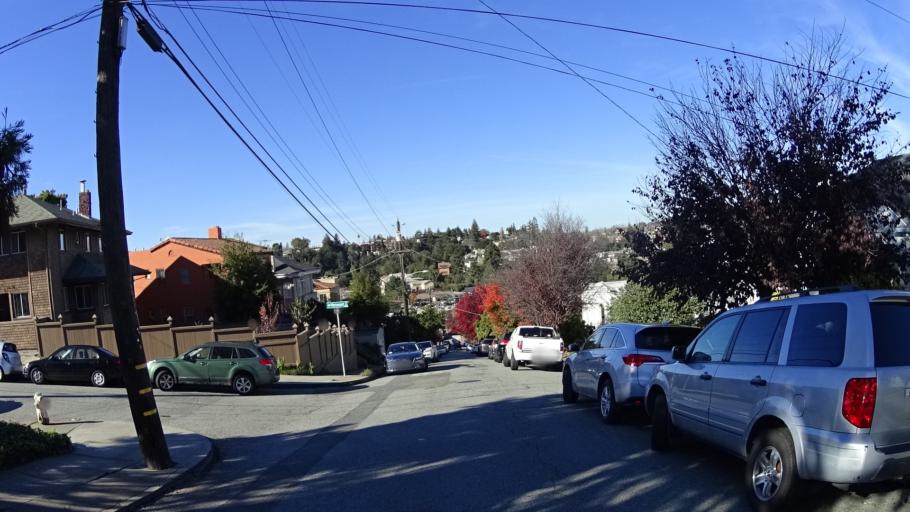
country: US
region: California
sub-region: Alameda County
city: Piedmont
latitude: 37.8168
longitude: -122.2424
